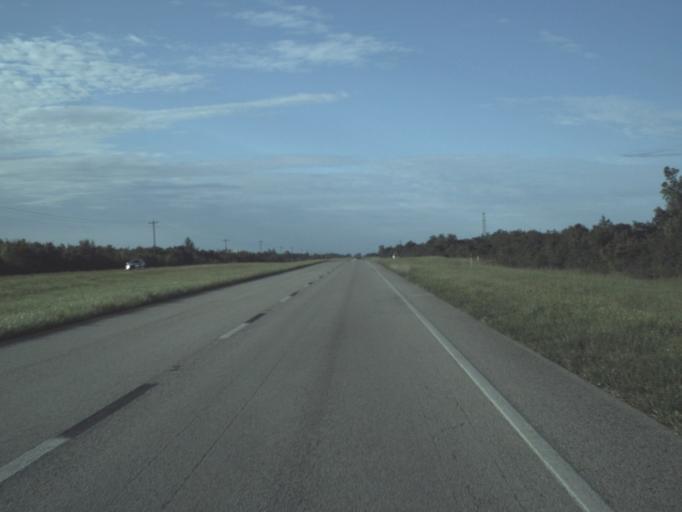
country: US
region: Florida
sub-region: Highlands County
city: Placid Lakes
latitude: 27.1338
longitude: -81.3296
